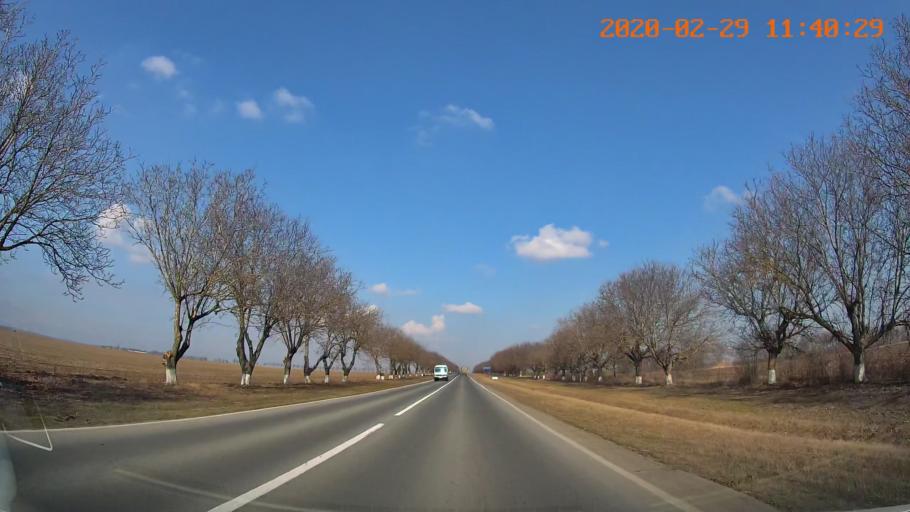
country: MD
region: Rezina
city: Saharna
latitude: 47.6570
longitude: 29.0200
